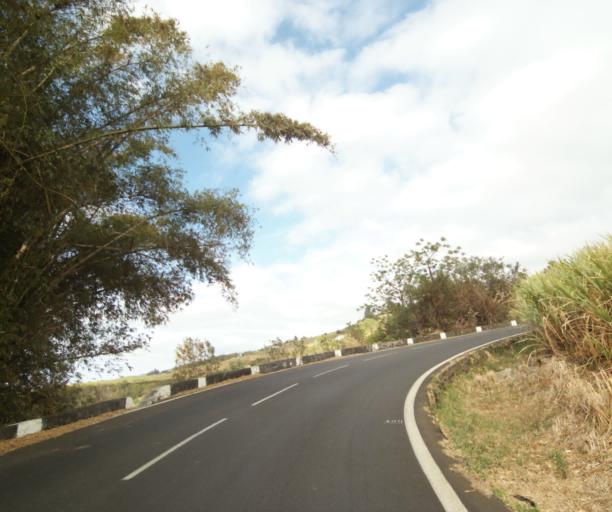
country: RE
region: Reunion
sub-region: Reunion
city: Saint-Paul
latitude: -21.0239
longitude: 55.3141
